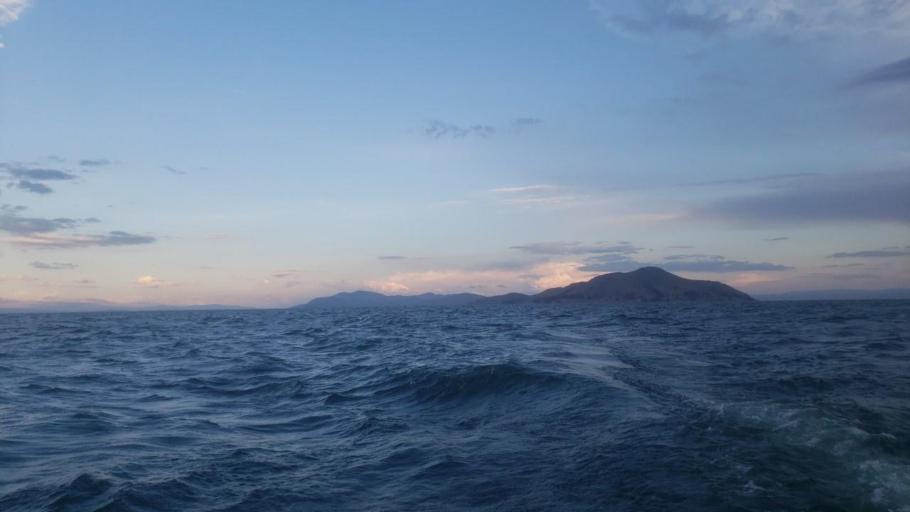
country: BO
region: La Paz
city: San Pedro
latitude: -16.2606
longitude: -68.8070
